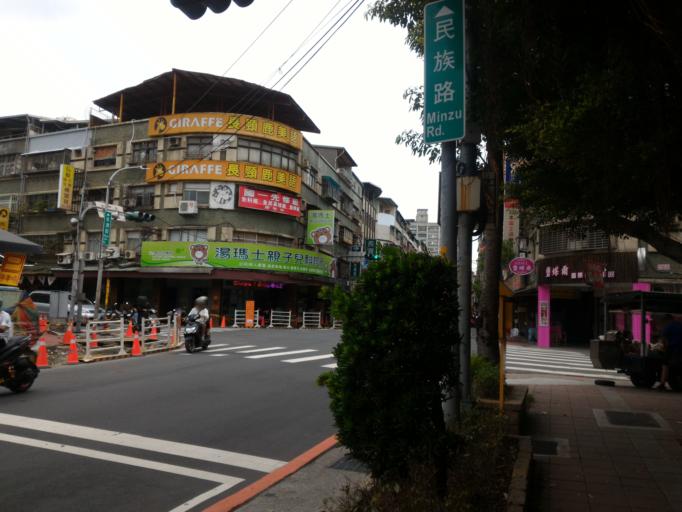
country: TW
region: Taipei
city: Taipei
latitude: 25.0909
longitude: 121.4702
